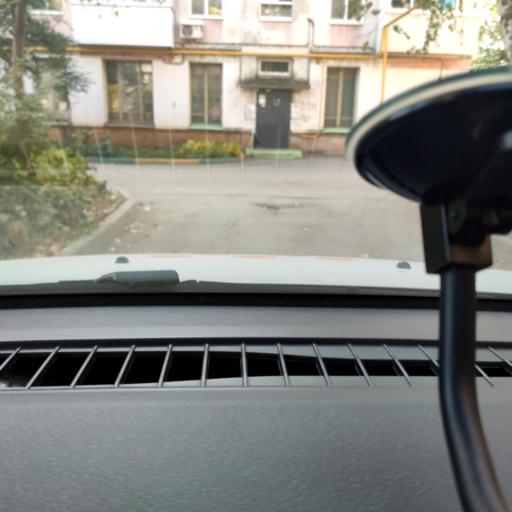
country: RU
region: Samara
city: Samara
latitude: 53.1878
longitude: 50.1827
